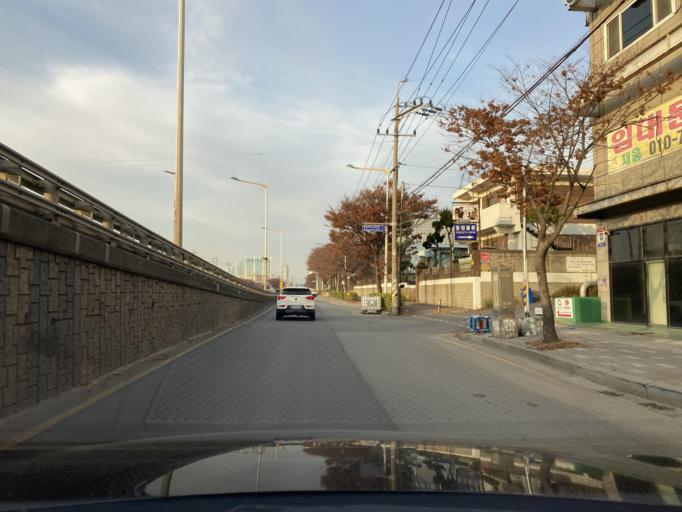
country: KR
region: Incheon
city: Incheon
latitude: 37.5005
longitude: 126.6484
